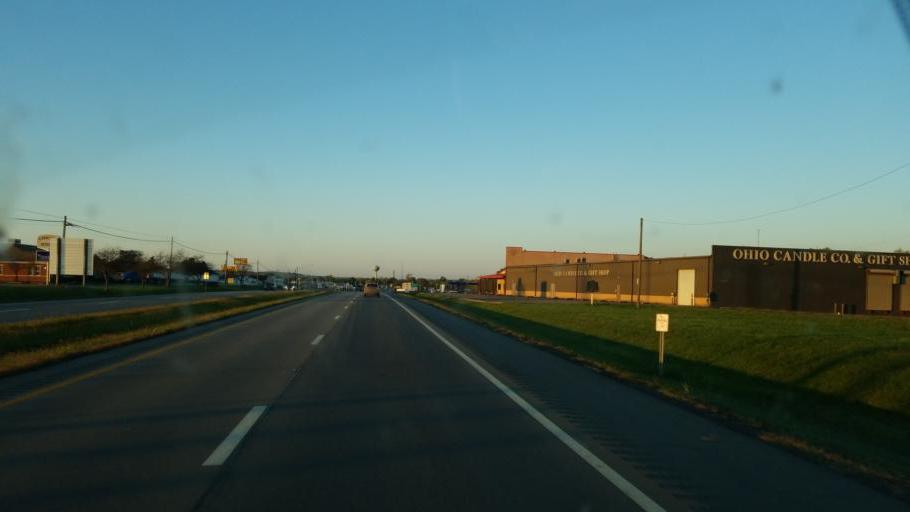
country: US
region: Ohio
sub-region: Pike County
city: Piketon
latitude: 39.0555
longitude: -83.0196
